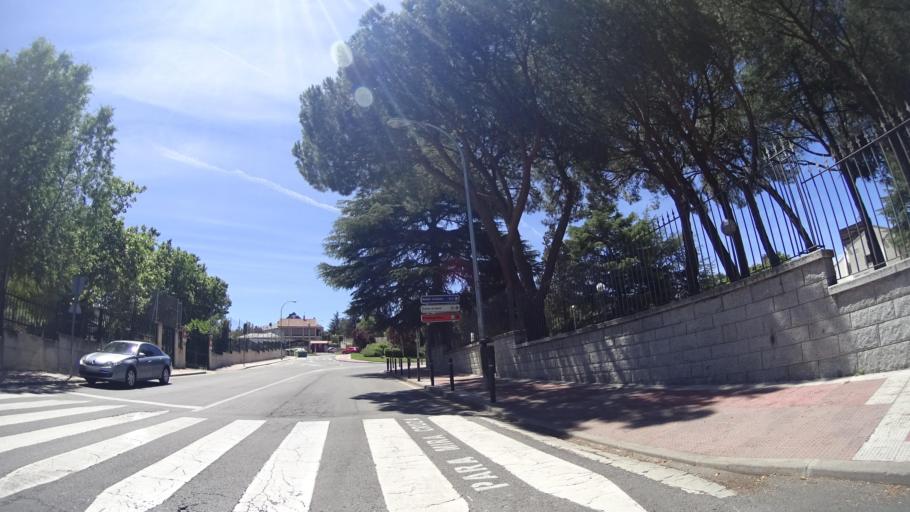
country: ES
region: Madrid
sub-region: Provincia de Madrid
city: Collado-Villalba
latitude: 40.6434
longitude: -3.9877
